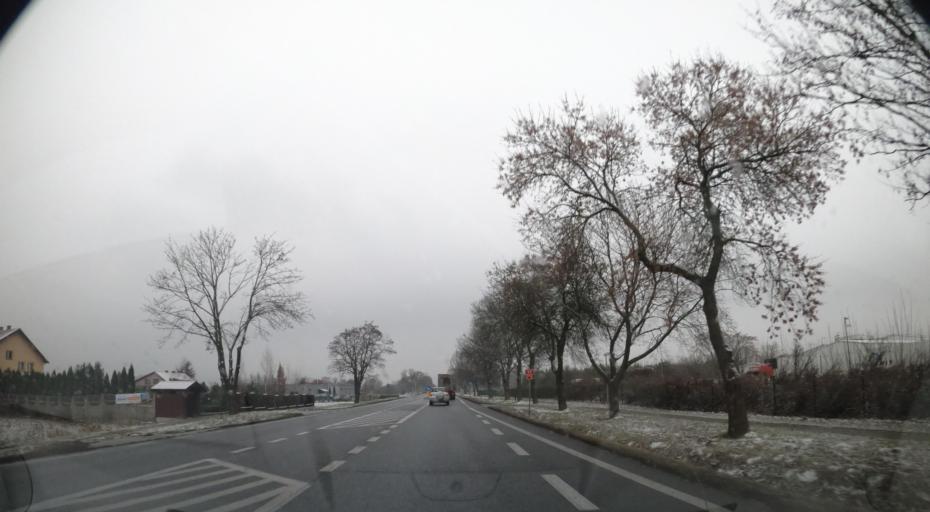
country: PL
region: Masovian Voivodeship
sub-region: Powiat sochaczewski
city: Teresin
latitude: 52.2212
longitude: 20.3290
